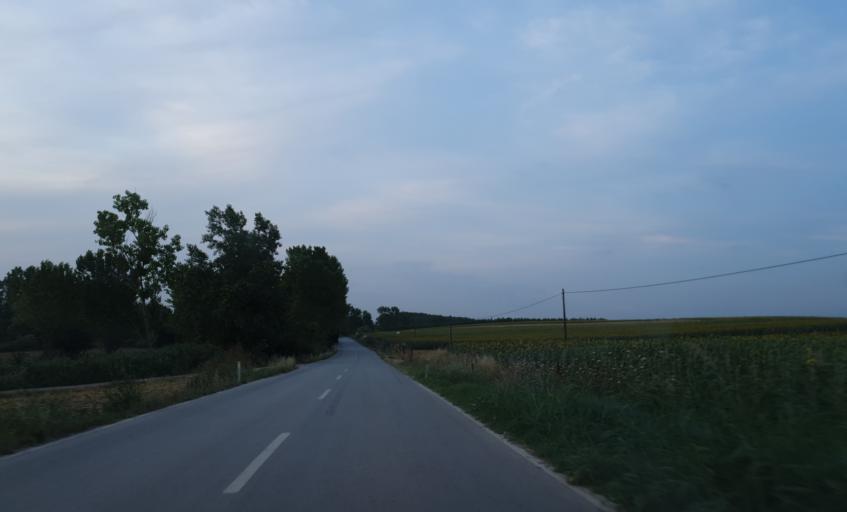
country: TR
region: Kirklareli
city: Buyukkaristiran
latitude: 41.3688
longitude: 27.6097
